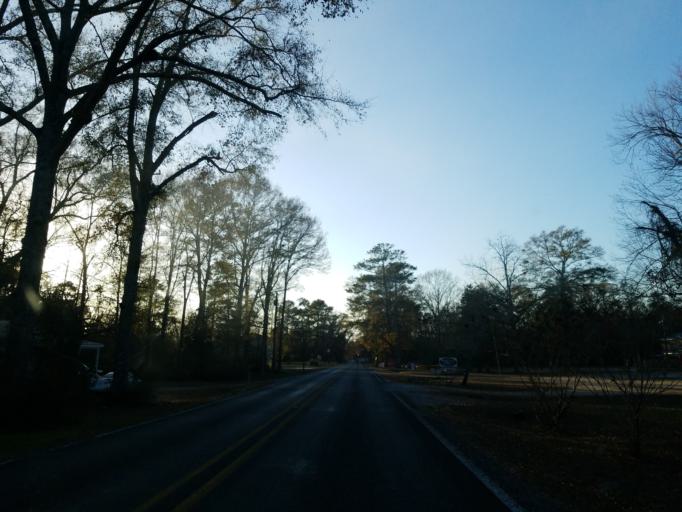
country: US
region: Mississippi
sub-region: Clarke County
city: Stonewall
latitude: 32.1758
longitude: -88.8249
